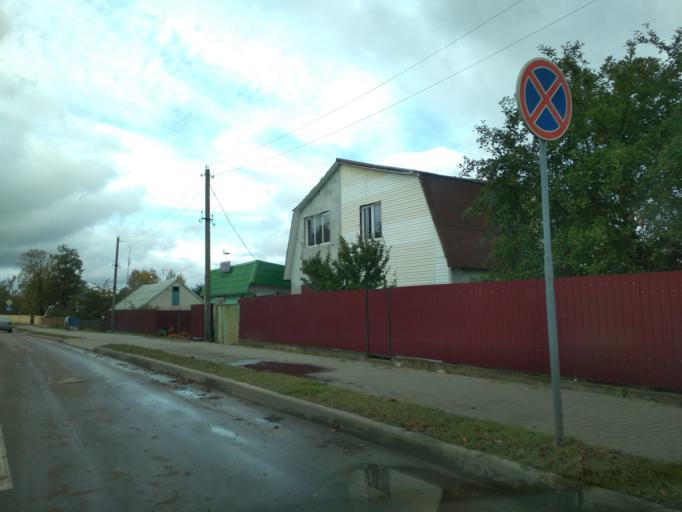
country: BY
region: Minsk
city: Mar''ina Horka
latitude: 53.5194
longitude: 28.1541
